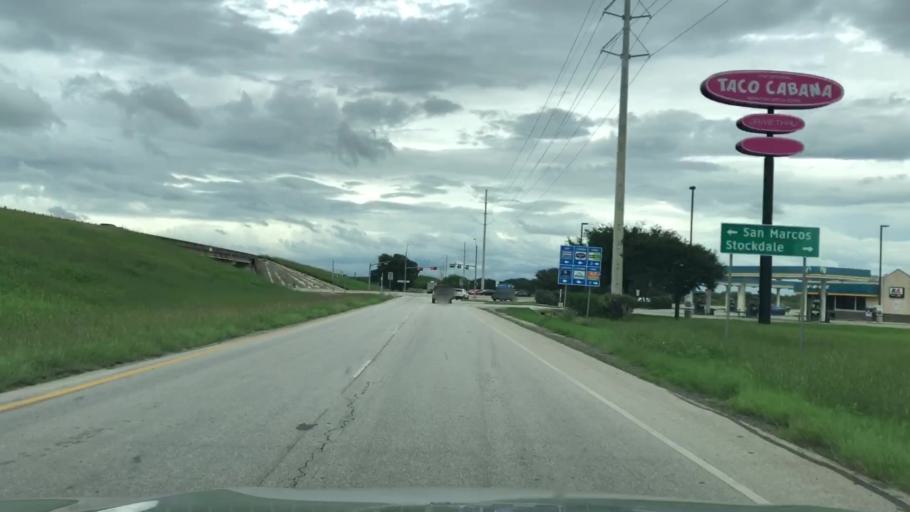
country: US
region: Texas
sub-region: Guadalupe County
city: Seguin
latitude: 29.5988
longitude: -97.9523
